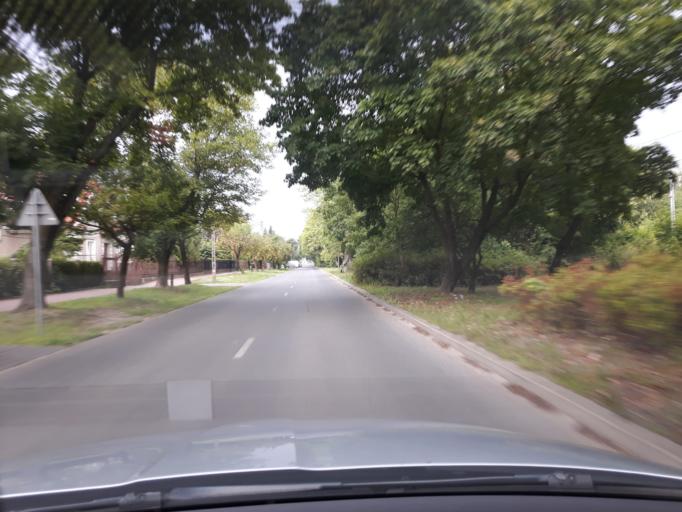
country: PL
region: Masovian Voivodeship
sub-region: Powiat wolominski
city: Zabki
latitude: 52.2951
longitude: 21.1202
